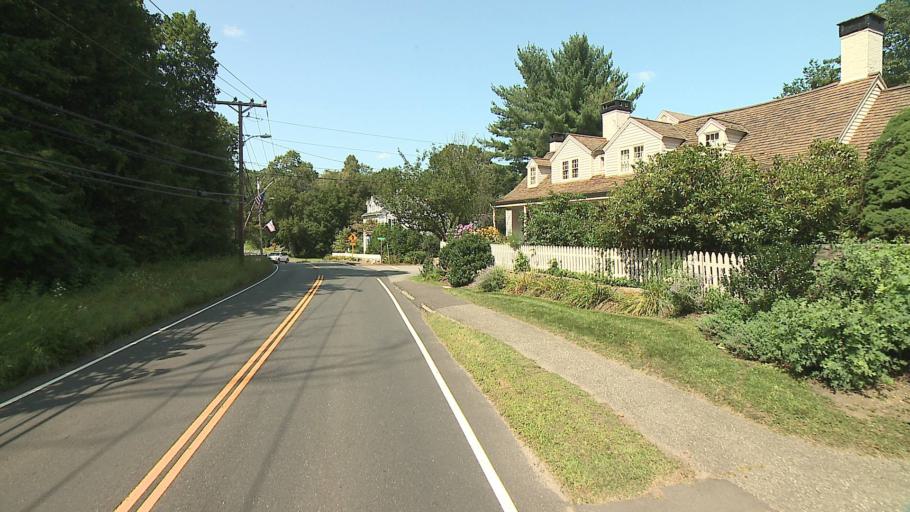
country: US
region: Connecticut
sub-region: Fairfield County
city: Danbury
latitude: 41.4688
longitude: -73.3890
